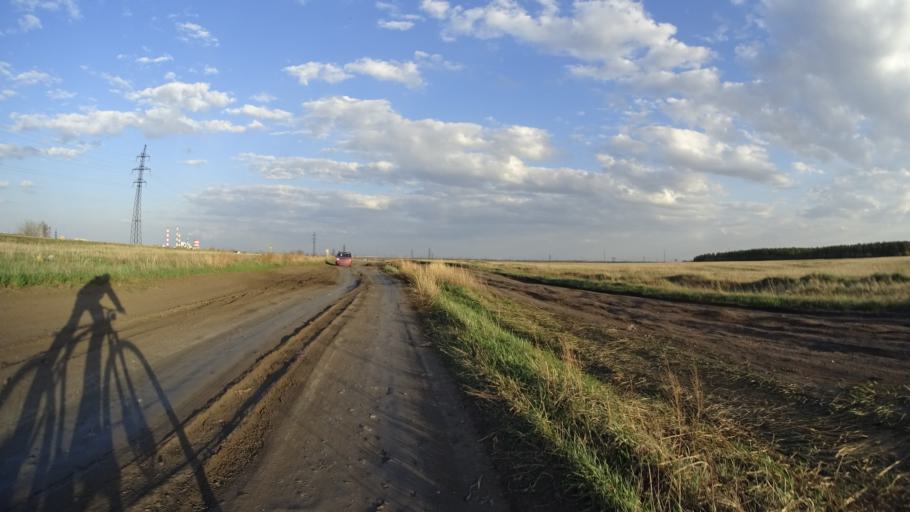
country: RU
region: Chelyabinsk
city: Troitsk
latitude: 54.0509
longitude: 61.5933
